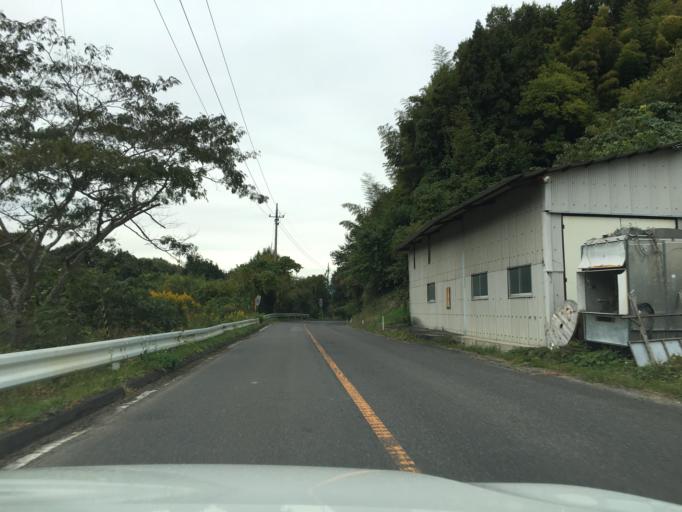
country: JP
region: Fukushima
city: Miharu
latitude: 37.4506
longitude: 140.5085
